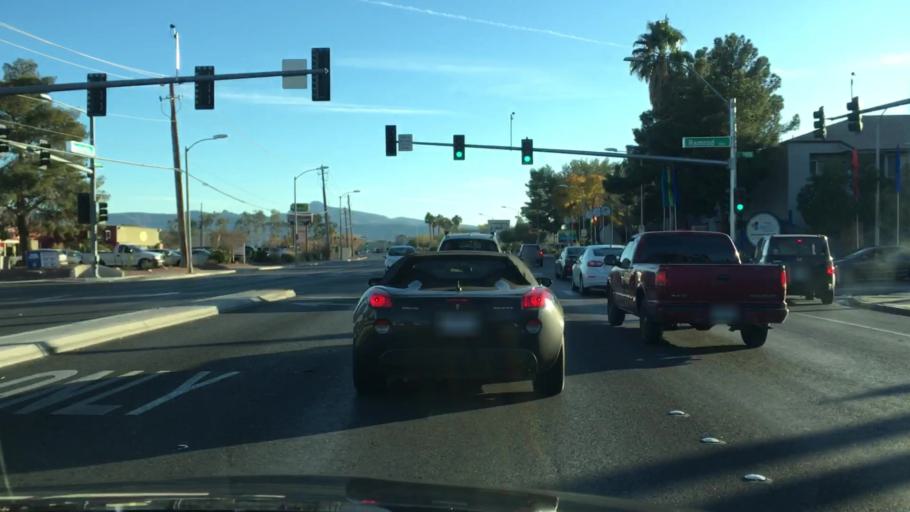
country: US
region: Nevada
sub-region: Clark County
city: Whitney
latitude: 36.0767
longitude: -115.0733
